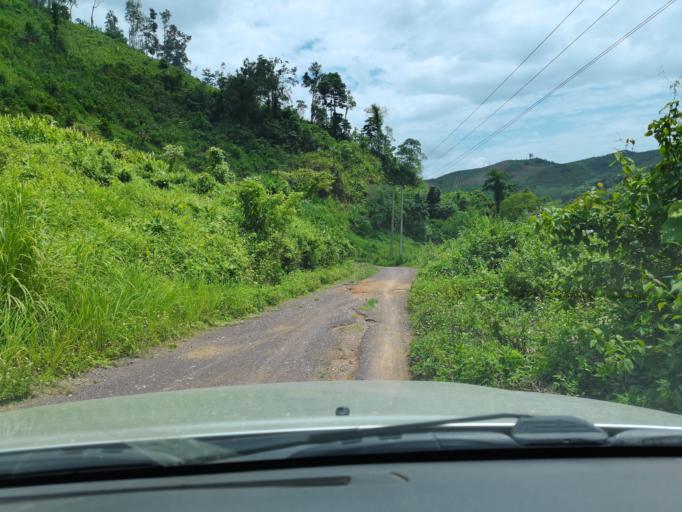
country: LA
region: Loungnamtha
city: Muang Long
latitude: 20.7120
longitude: 101.0126
